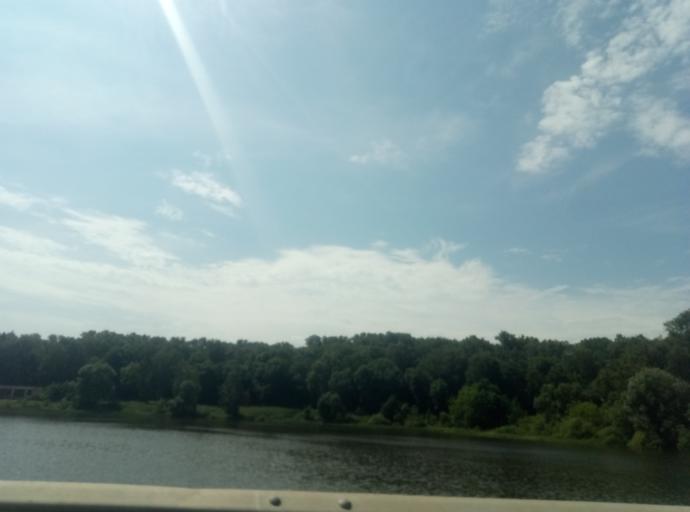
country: RU
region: Tula
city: Kireyevsk
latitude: 53.9327
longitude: 37.9416
